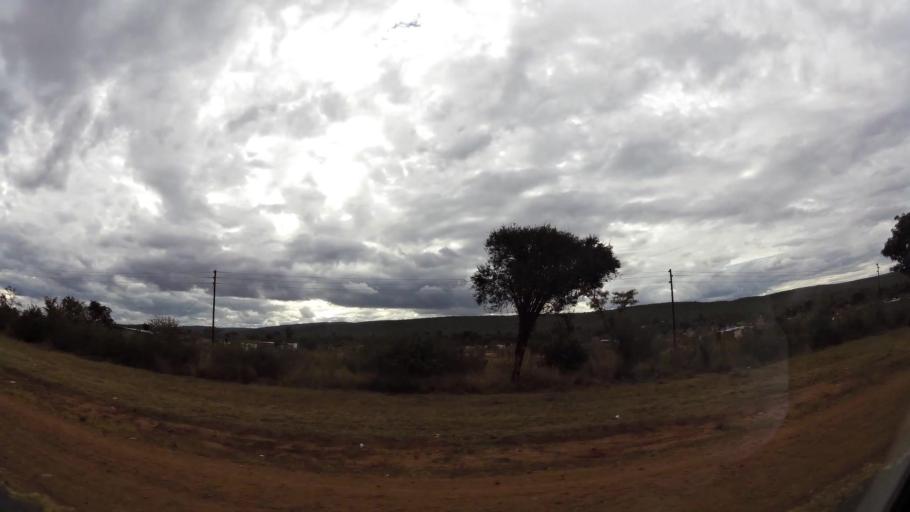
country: ZA
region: Limpopo
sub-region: Waterberg District Municipality
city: Modimolle
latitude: -24.6819
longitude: 28.4313
